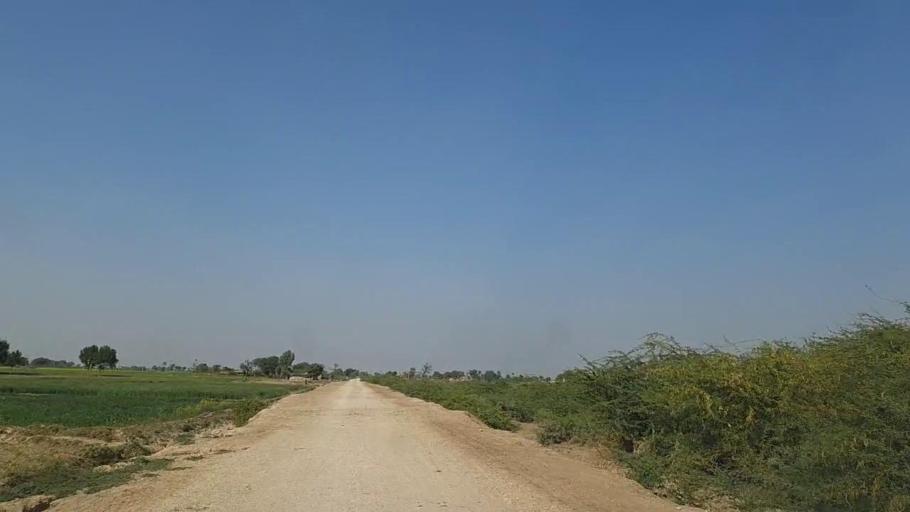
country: PK
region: Sindh
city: Naukot
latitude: 24.9033
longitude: 69.4259
